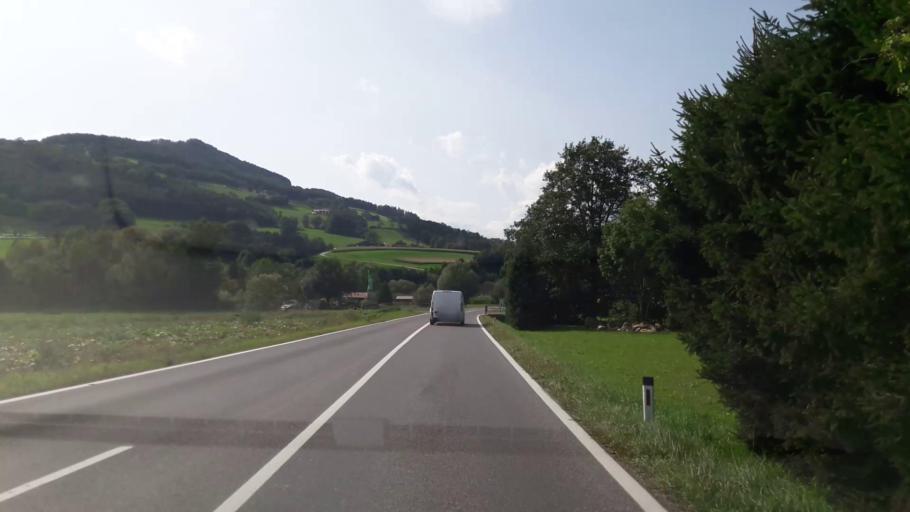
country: AT
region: Styria
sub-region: Politischer Bezirk Hartberg-Fuerstenfeld
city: Stubenberg
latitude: 47.2353
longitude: 15.8020
